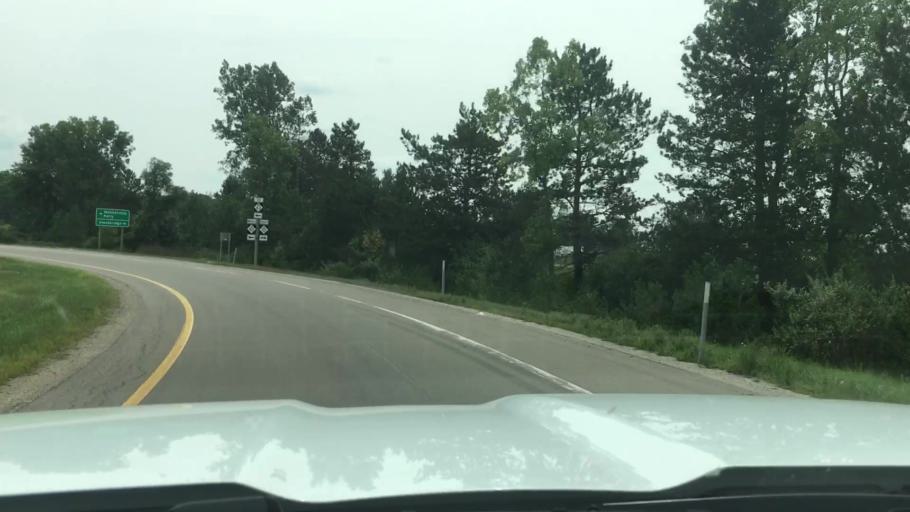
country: US
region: Michigan
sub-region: Ingham County
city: Webberville
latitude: 42.6579
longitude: -84.2001
